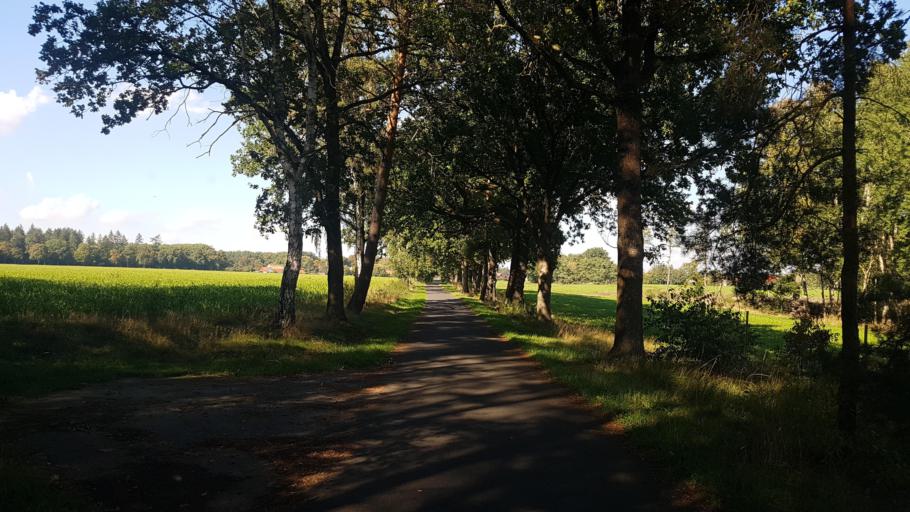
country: DE
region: Brandenburg
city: Ihlow
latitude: 51.8752
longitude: 13.2476
